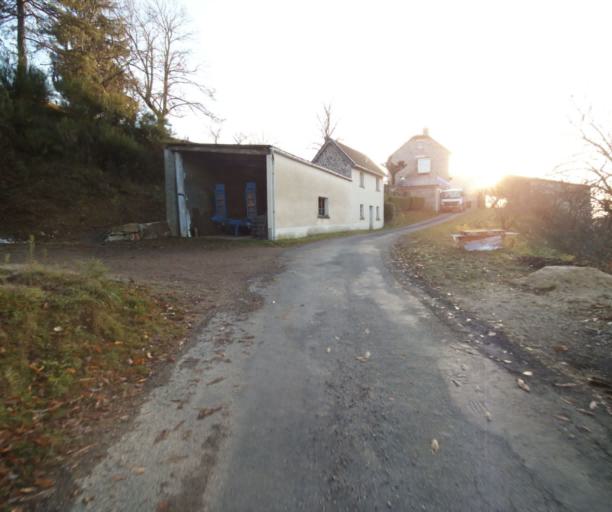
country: FR
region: Limousin
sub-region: Departement de la Correze
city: Laguenne
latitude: 45.2351
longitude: 1.8168
